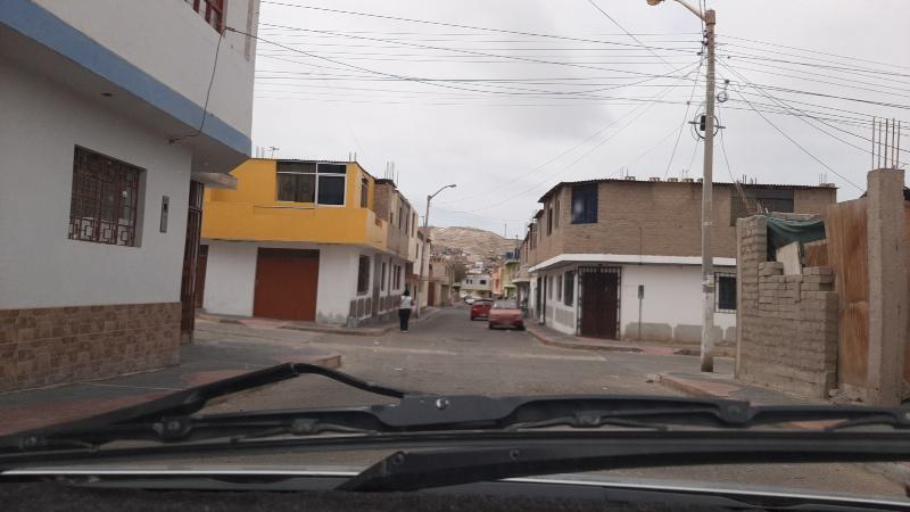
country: PE
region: Moquegua
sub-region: Provincia de Ilo
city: Ilo
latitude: -17.6522
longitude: -71.3419
